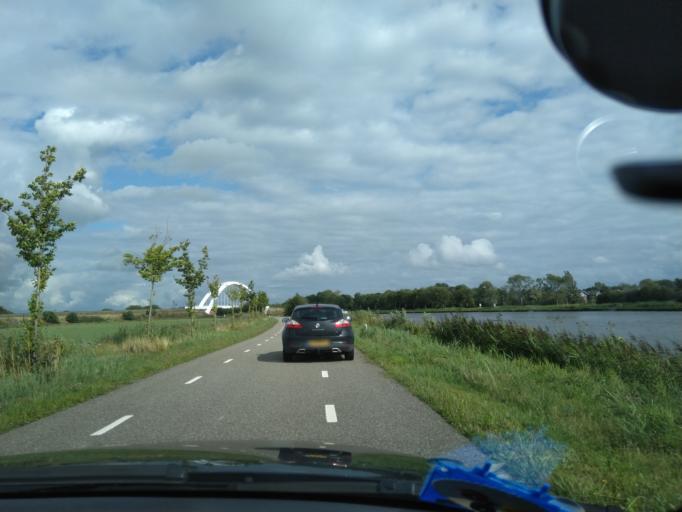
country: NL
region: Groningen
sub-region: Gemeente Zuidhorn
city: Noordhorn
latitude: 53.2533
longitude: 6.3825
